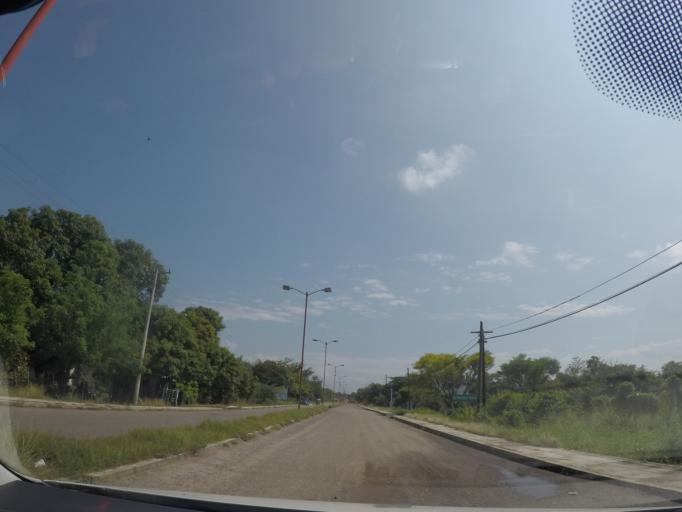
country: MX
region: Oaxaca
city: San Francisco Ixhuatan
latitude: 16.3925
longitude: -94.4583
